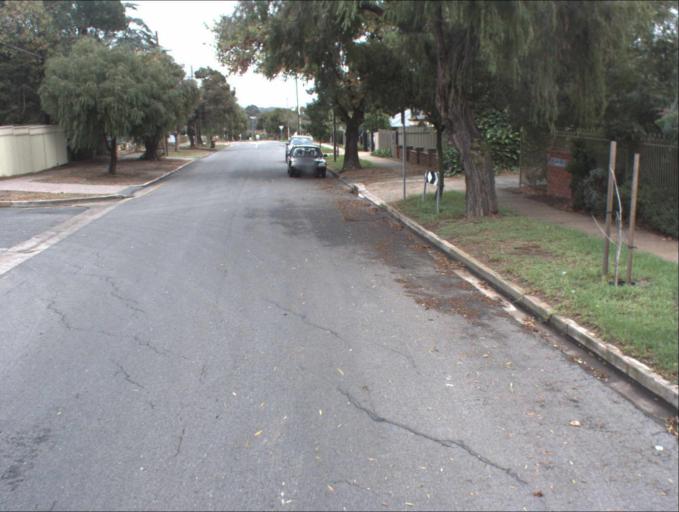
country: AU
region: South Australia
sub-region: Port Adelaide Enfield
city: Blair Athol
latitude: -34.8702
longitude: 138.5967
